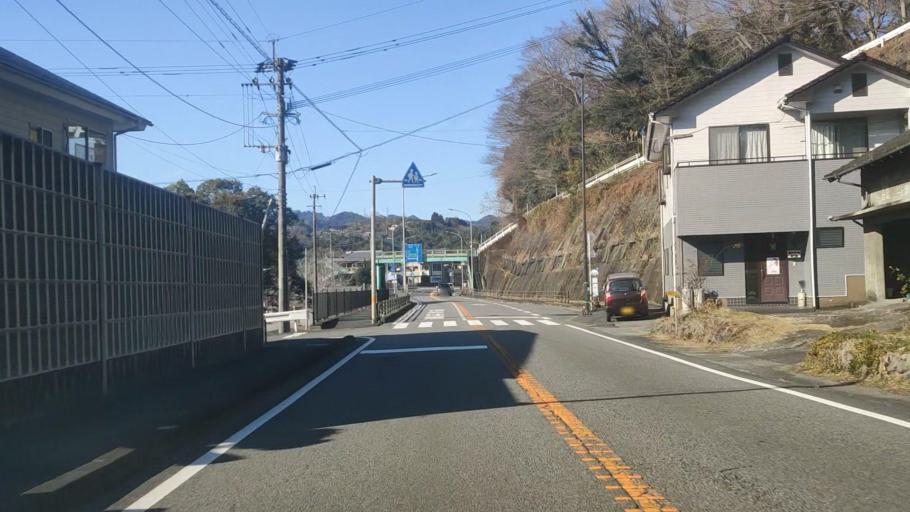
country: JP
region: Oita
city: Oita
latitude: 33.0707
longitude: 131.6397
